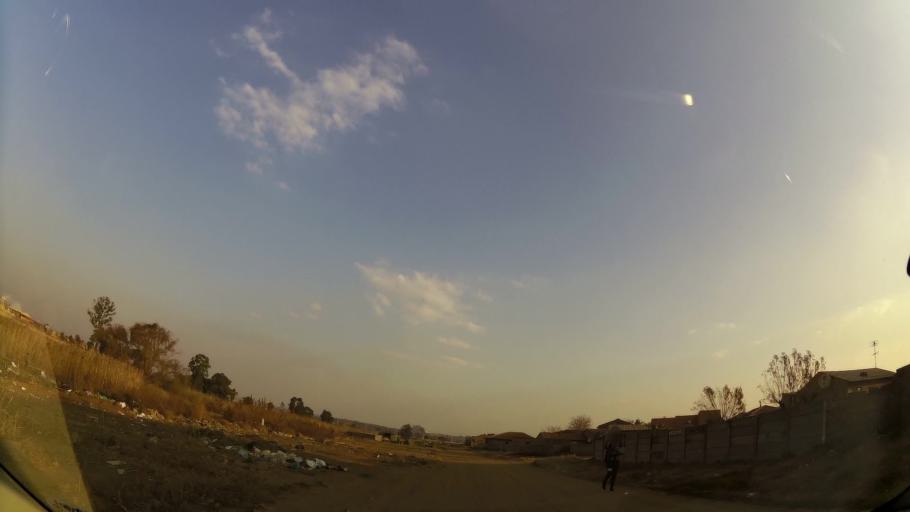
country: ZA
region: Gauteng
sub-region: Ekurhuleni Metropolitan Municipality
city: Benoni
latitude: -26.1594
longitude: 28.3833
